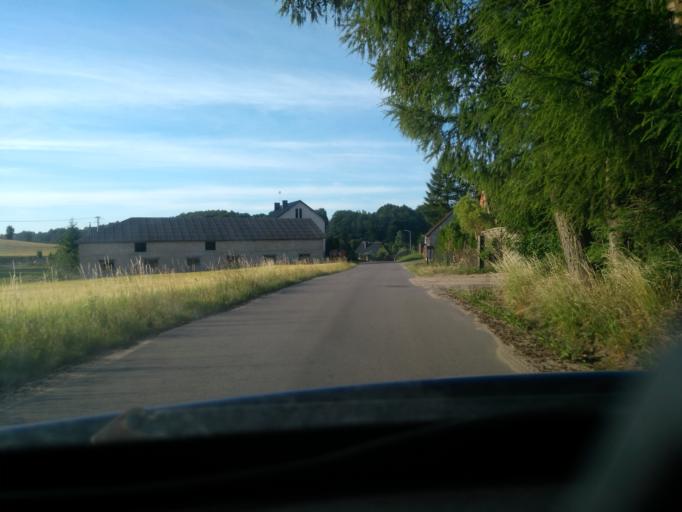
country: PL
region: Pomeranian Voivodeship
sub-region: Powiat kartuski
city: Przodkowo
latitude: 54.3821
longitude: 18.3169
